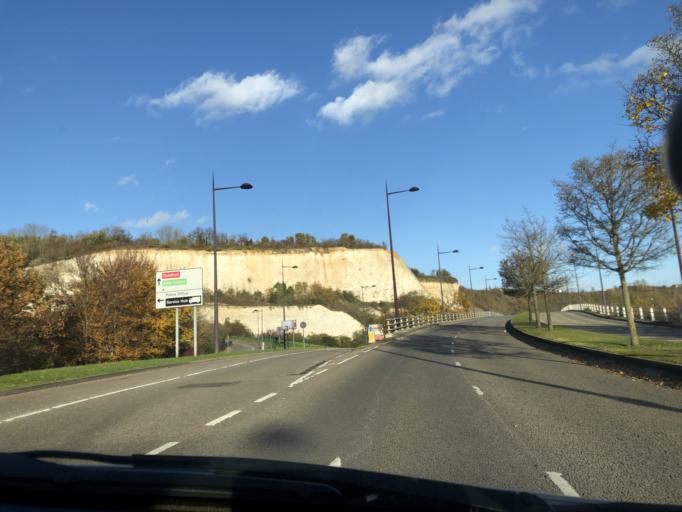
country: GB
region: England
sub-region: Kent
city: Stone
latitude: 51.4418
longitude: 0.2661
